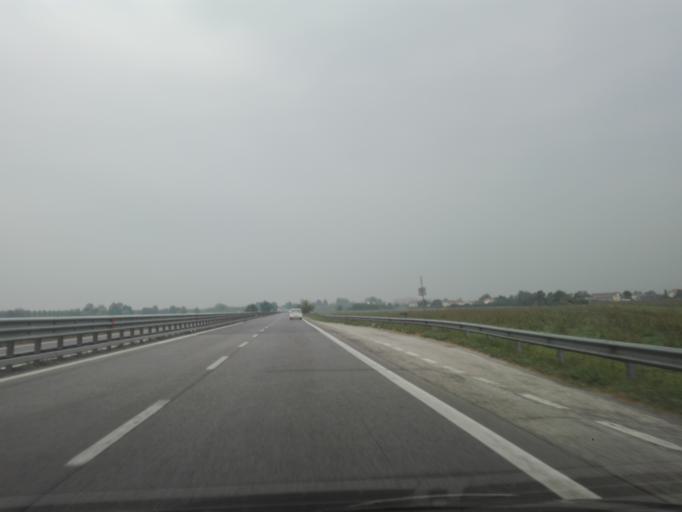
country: IT
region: Veneto
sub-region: Provincia di Verona
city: Legnago
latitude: 45.1692
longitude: 11.2956
